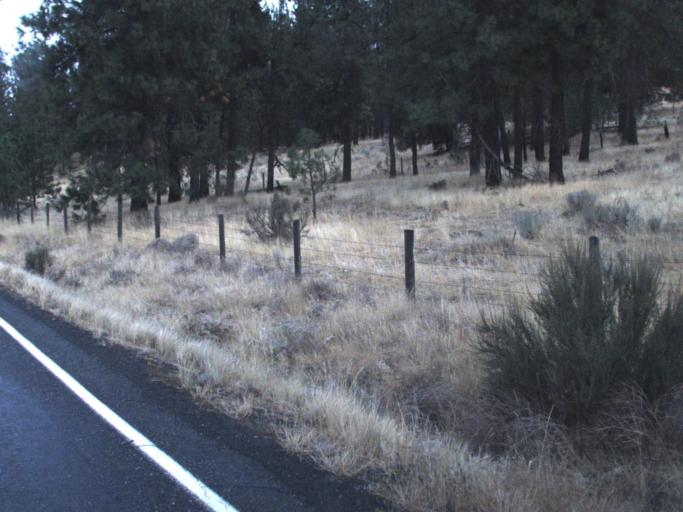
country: US
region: Washington
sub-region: Lincoln County
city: Davenport
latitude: 47.8032
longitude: -117.8924
